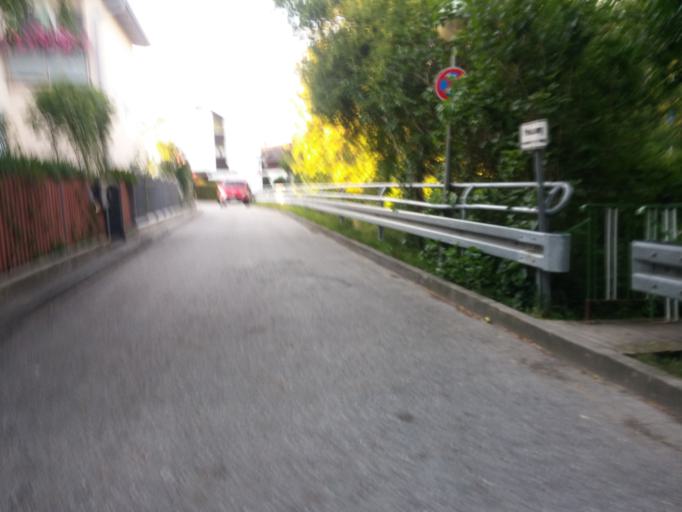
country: DE
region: Bavaria
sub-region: Upper Bavaria
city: Markt Schwaben
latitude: 48.1938
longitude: 11.8684
